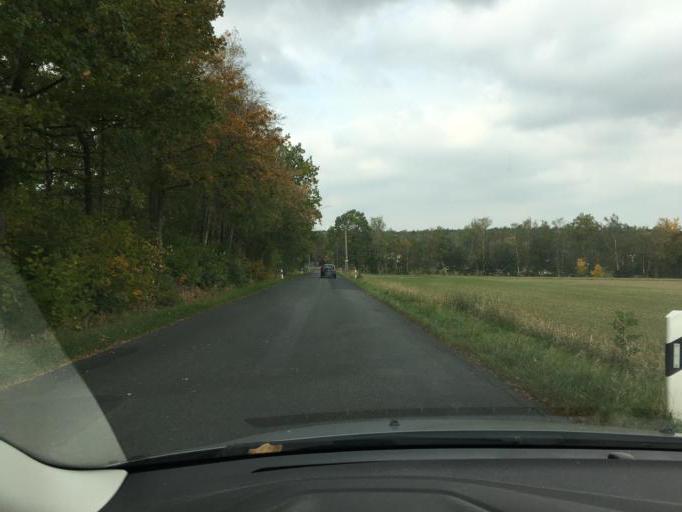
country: DE
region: Saxony
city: Freital
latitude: 50.9922
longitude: 13.6798
